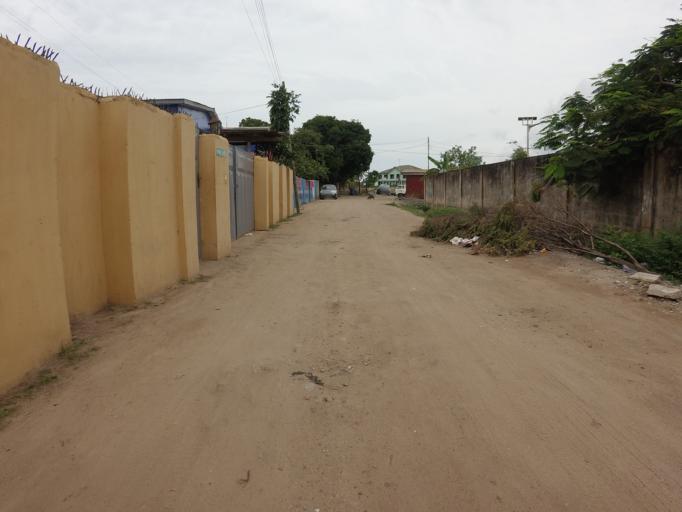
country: GH
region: Greater Accra
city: Accra
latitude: 5.5875
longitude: -0.2165
